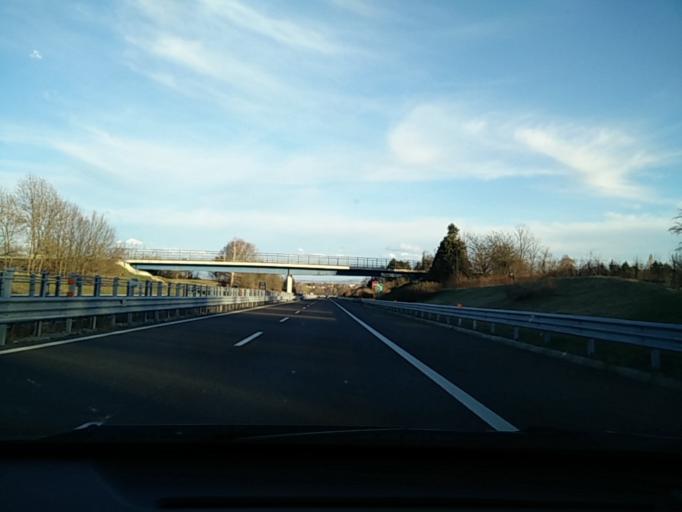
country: IT
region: Friuli Venezia Giulia
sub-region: Provincia di Udine
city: Pagnacco
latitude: 46.1330
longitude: 13.1886
